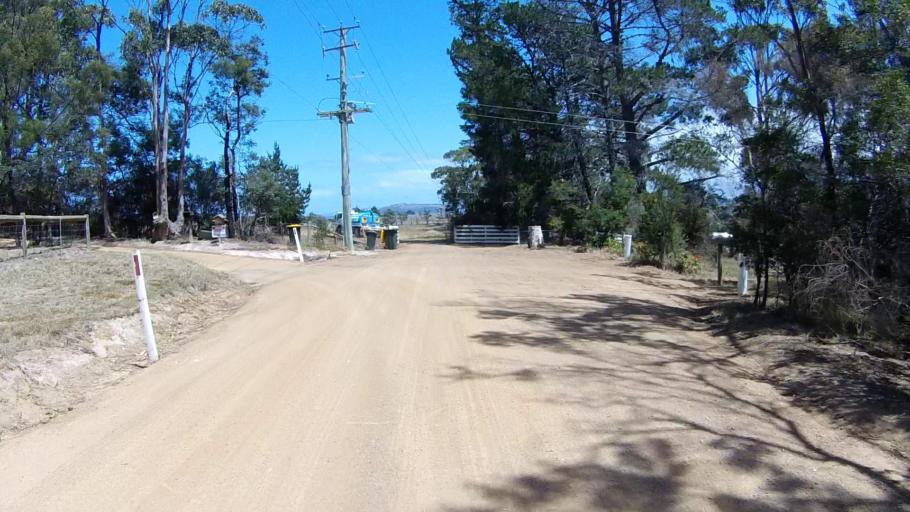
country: AU
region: Tasmania
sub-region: Clarence
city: Lauderdale
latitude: -42.9426
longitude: 147.4608
